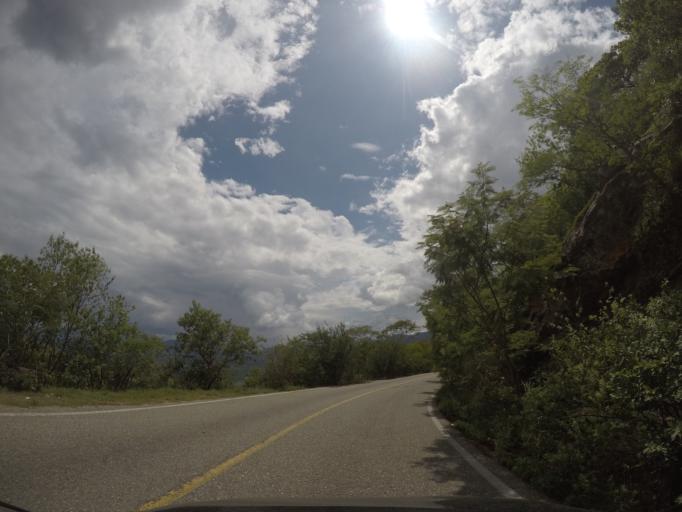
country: MX
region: Oaxaca
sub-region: San Jeronimo Coatlan
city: San Cristobal Honduras
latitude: 16.4309
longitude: -97.0446
